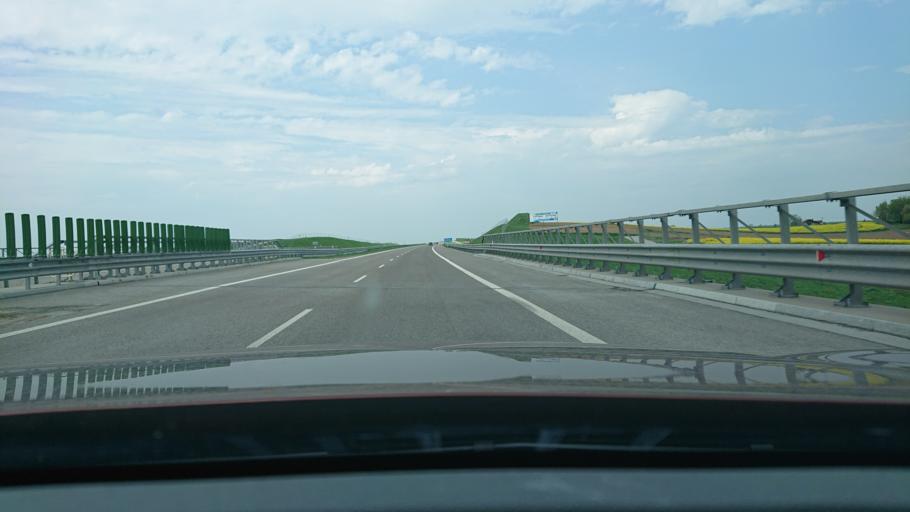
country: PL
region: Subcarpathian Voivodeship
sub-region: Powiat jaroslawski
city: Pawlosiow
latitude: 49.9523
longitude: 22.6624
